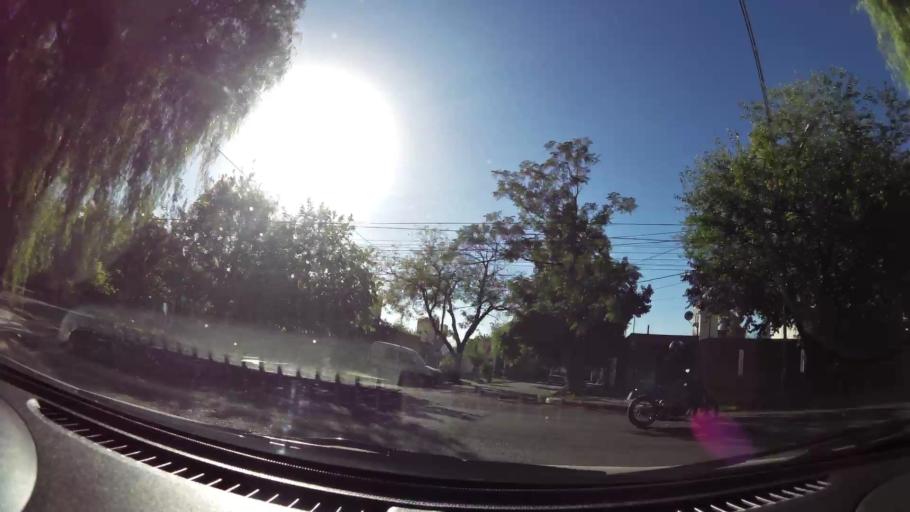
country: AR
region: Mendoza
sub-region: Departamento de Godoy Cruz
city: Godoy Cruz
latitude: -32.9384
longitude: -68.8338
